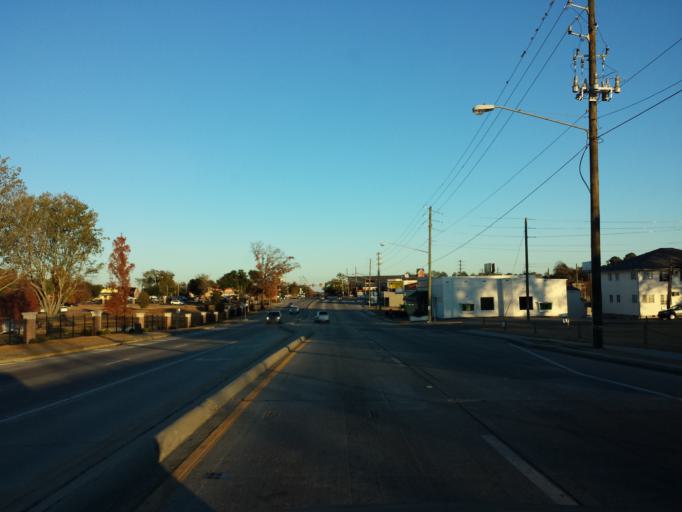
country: US
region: Mississippi
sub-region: Forrest County
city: Hattiesburg
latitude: 31.3247
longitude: -89.3319
